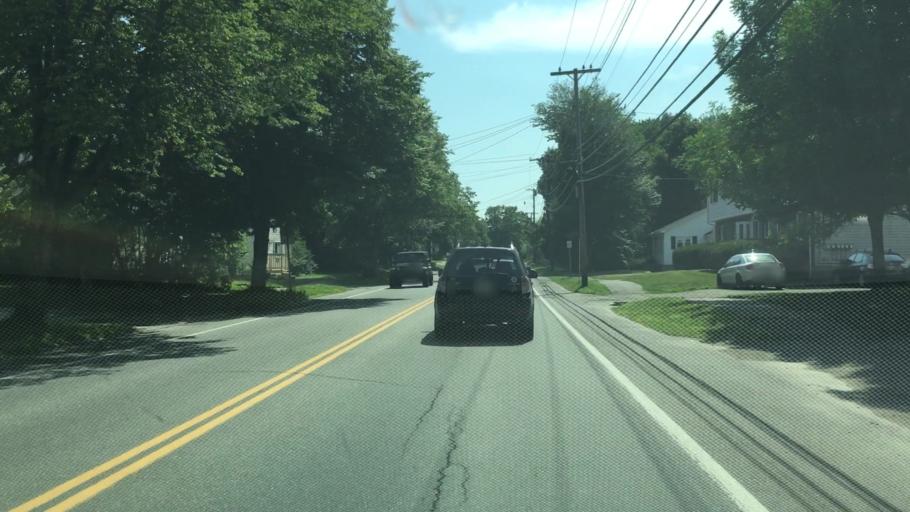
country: US
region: Maine
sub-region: Penobscot County
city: Brewer
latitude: 44.8174
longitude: -68.7642
